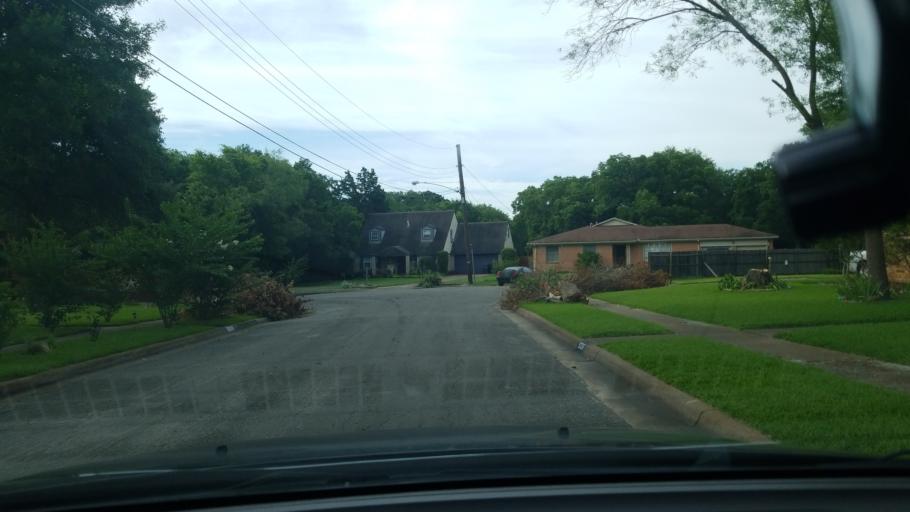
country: US
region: Texas
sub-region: Dallas County
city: Balch Springs
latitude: 32.7536
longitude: -96.6635
